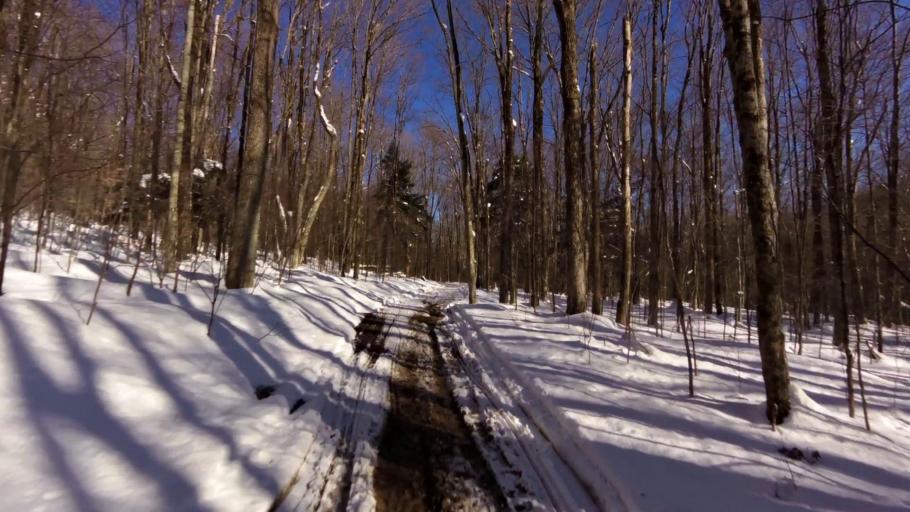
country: US
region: New York
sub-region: Cattaraugus County
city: Salamanca
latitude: 42.0214
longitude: -78.7891
